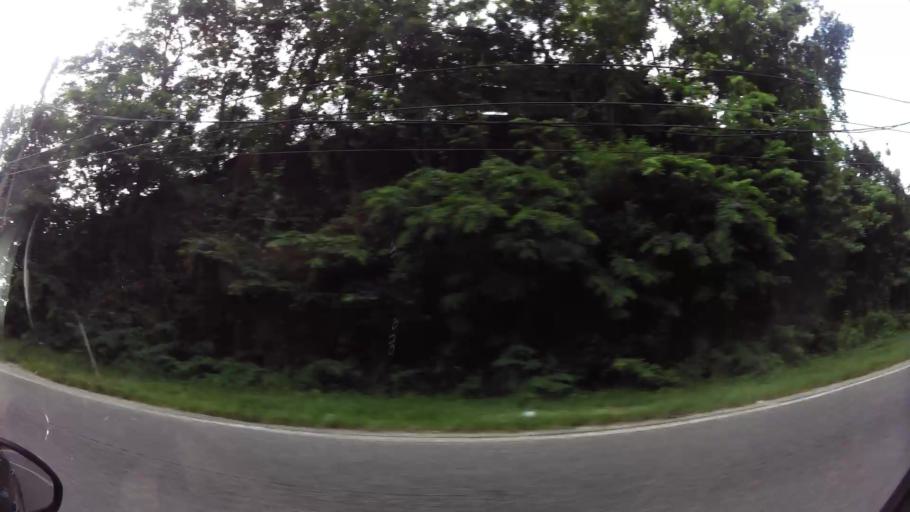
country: TT
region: San Juan/Laventille
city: Laventille
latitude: 10.6742
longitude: -61.4934
